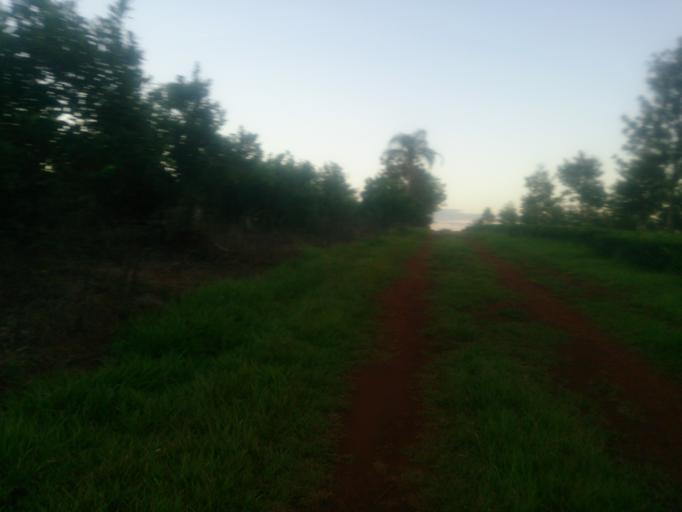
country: AR
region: Misiones
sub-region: Departamento de Obera
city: Obera
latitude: -27.4465
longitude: -55.0920
